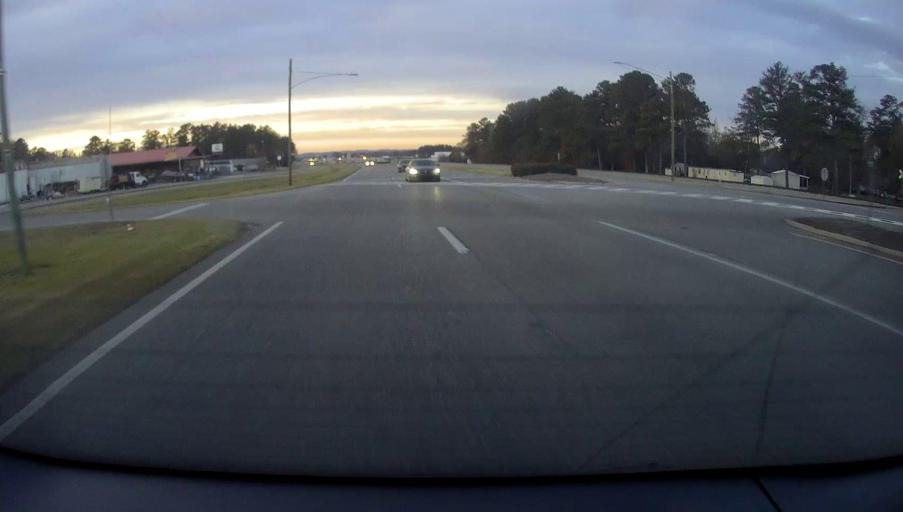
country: US
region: Alabama
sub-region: Etowah County
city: Glencoe
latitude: 33.9589
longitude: -85.9349
